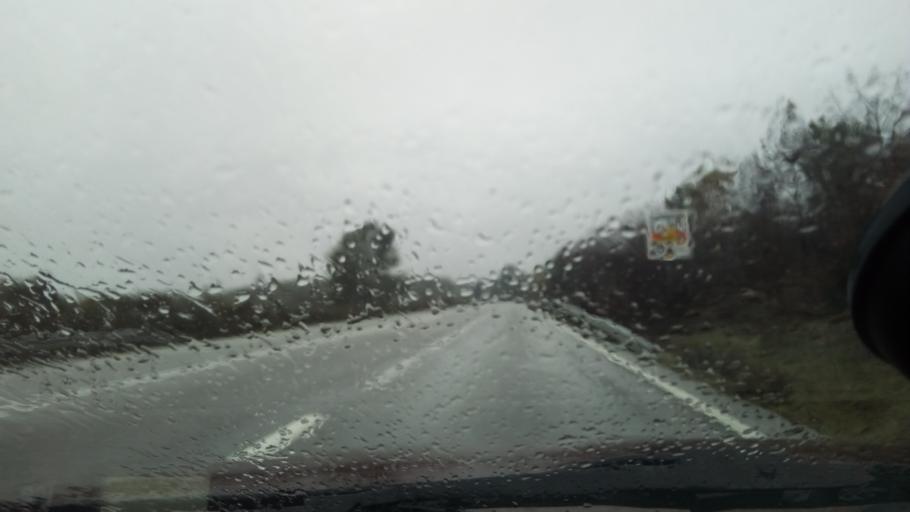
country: PT
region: Guarda
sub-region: Fornos de Algodres
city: Fornos de Algodres
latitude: 40.6028
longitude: -7.5601
